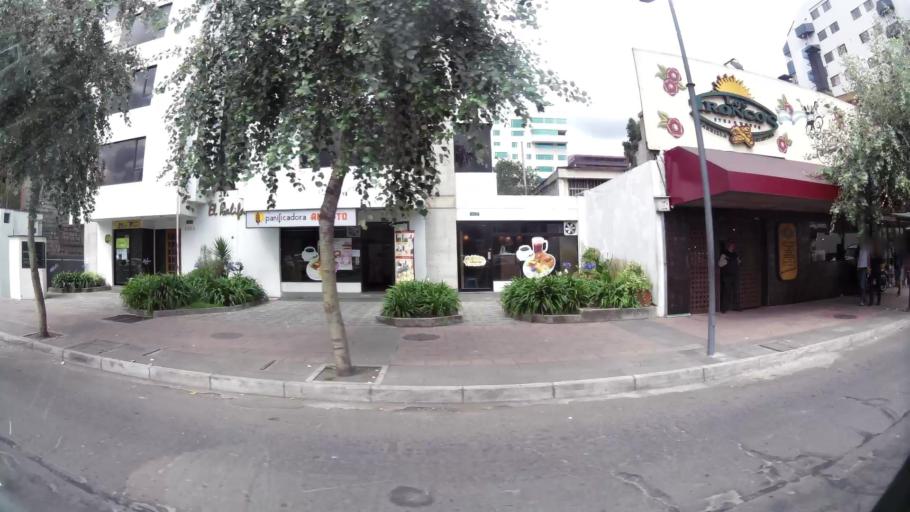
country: EC
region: Pichincha
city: Quito
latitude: -0.1807
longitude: -78.4816
